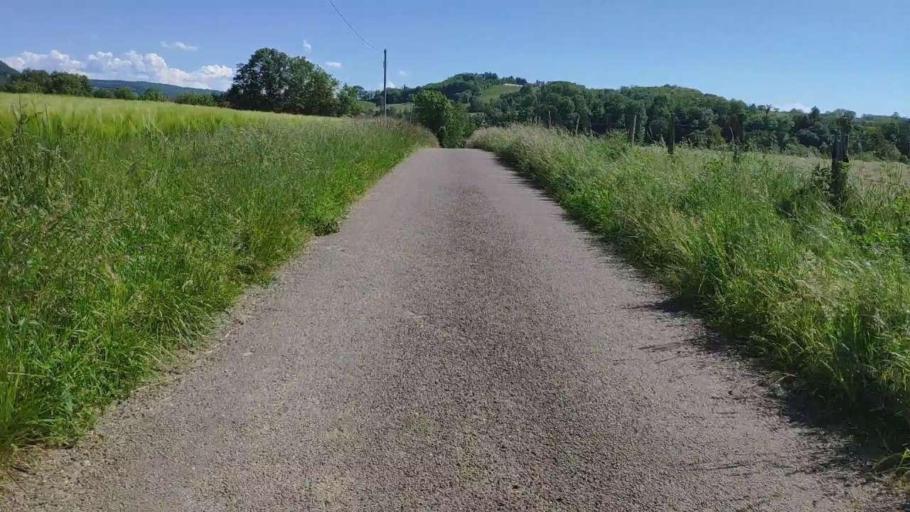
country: FR
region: Franche-Comte
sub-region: Departement du Jura
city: Perrigny
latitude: 46.7356
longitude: 5.5834
